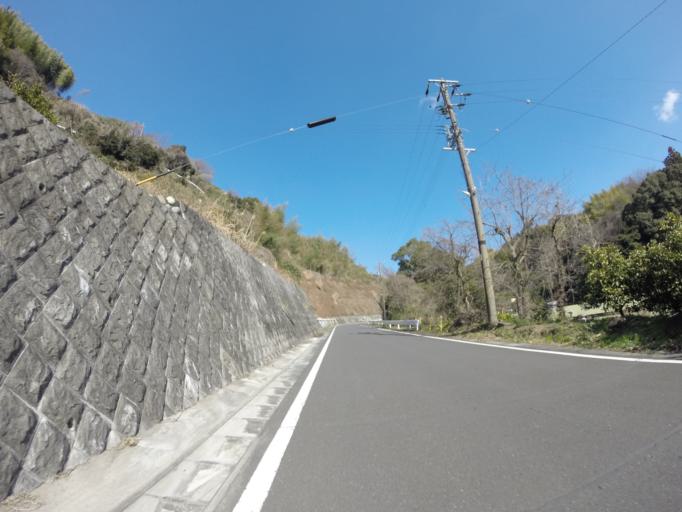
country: JP
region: Shizuoka
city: Shizuoka-shi
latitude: 35.0712
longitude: 138.4933
